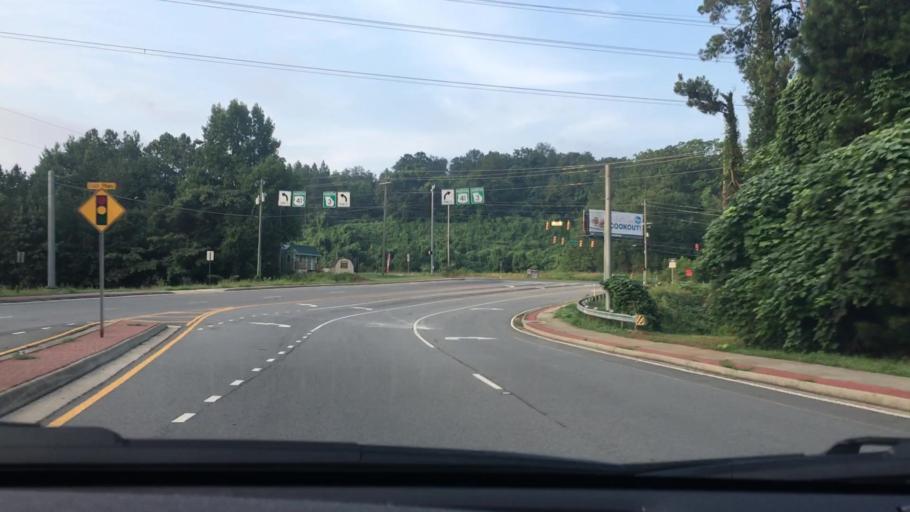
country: US
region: Georgia
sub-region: Cobb County
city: Kennesaw
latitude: 33.9949
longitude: -84.5811
